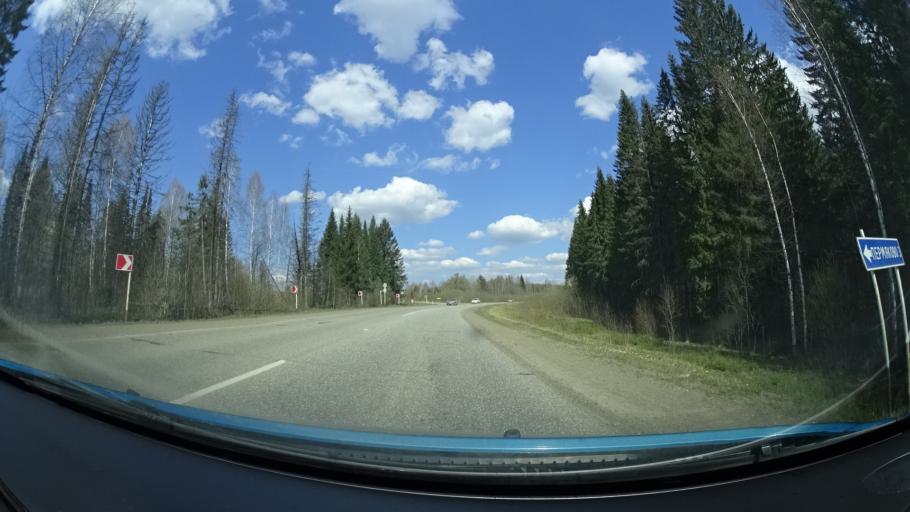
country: RU
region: Perm
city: Osa
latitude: 57.3904
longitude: 55.6089
